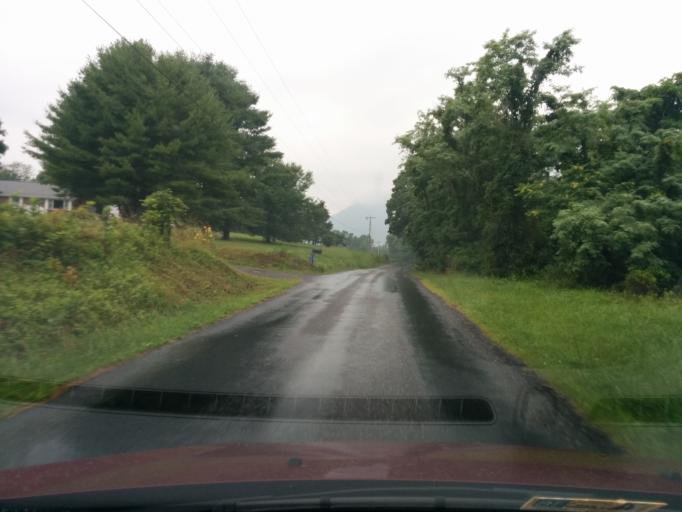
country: US
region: Virginia
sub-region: Rockbridge County
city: East Lexington
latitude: 37.8746
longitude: -79.4344
